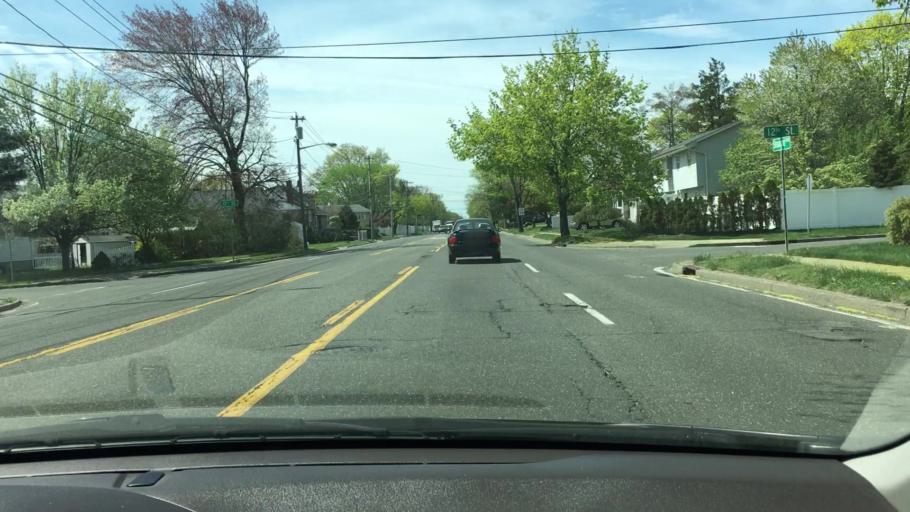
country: US
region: New York
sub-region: Suffolk County
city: North Lindenhurst
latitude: 40.7216
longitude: -73.3777
